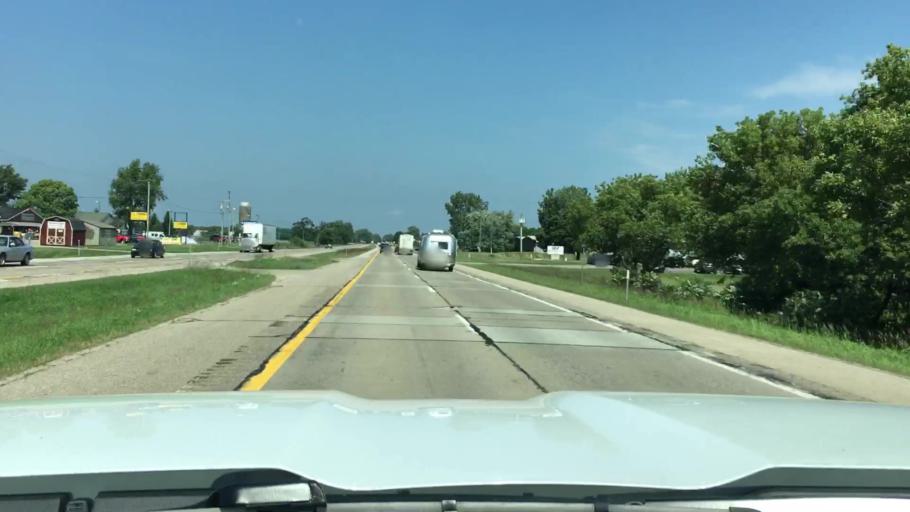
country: US
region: Michigan
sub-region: Kalamazoo County
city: Schoolcraft
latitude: 42.0958
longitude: -85.6367
